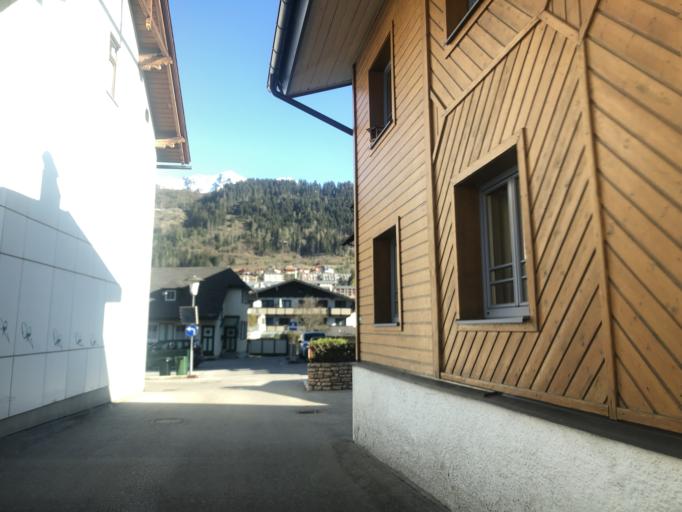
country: AT
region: Styria
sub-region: Politischer Bezirk Liezen
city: Schladming
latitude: 47.3925
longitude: 13.6865
